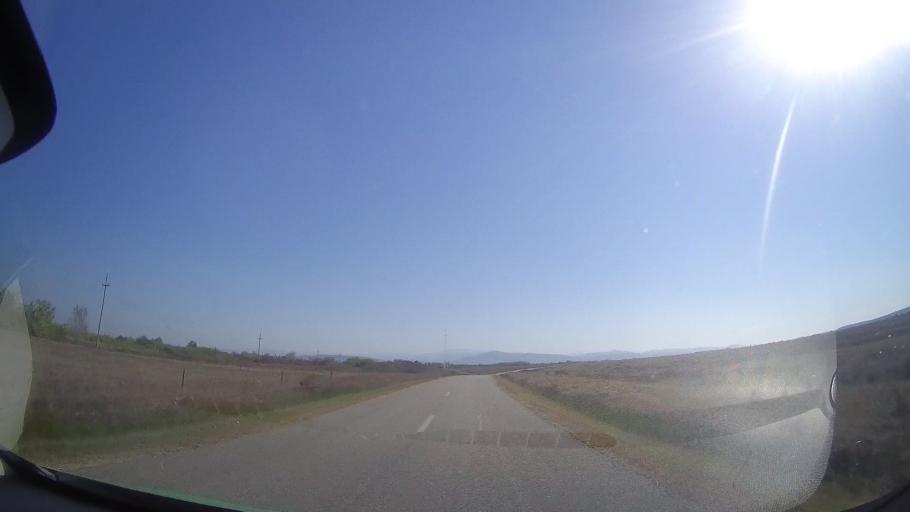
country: RO
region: Timis
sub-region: Comuna Traian Vuia
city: Traian Vuia
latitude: 45.8017
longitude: 22.0062
